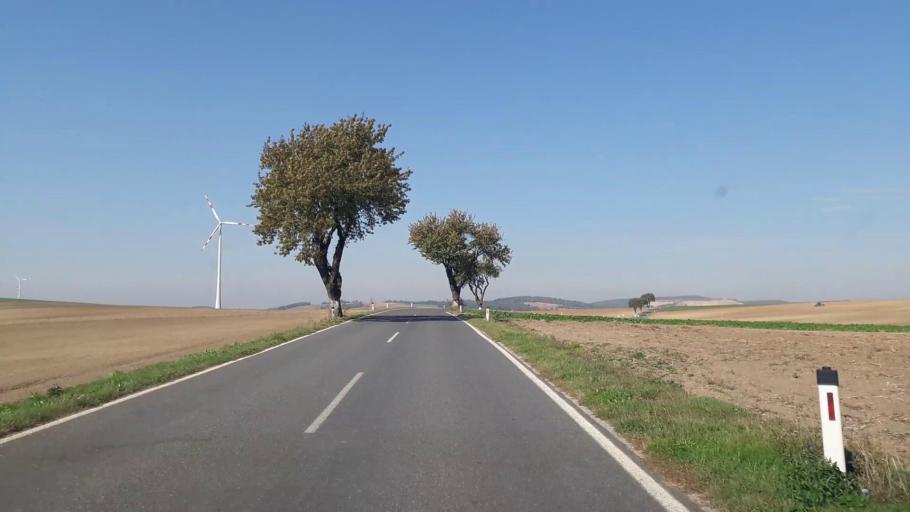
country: AT
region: Lower Austria
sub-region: Politischer Bezirk Korneuburg
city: Ernstbrunn
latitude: 48.5000
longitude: 16.3641
